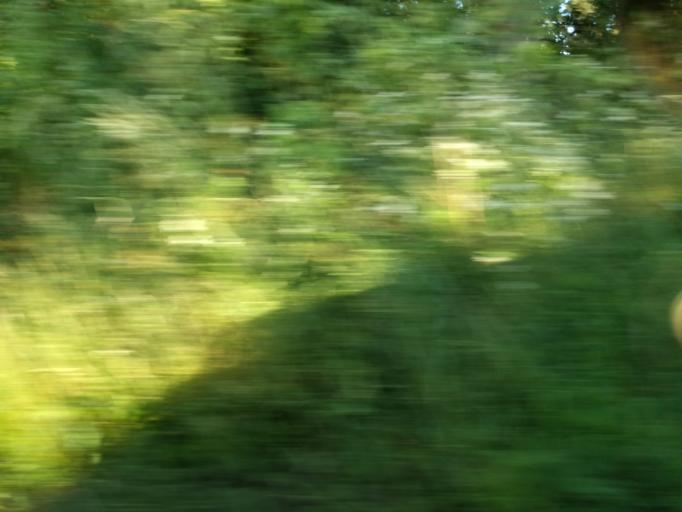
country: DK
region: South Denmark
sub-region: Kerteminde Kommune
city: Kerteminde
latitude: 55.5741
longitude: 10.6451
